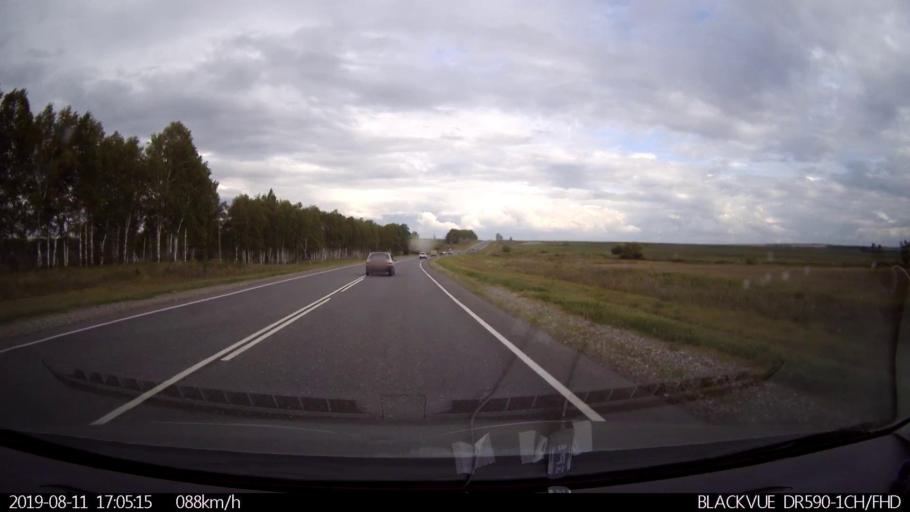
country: RU
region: Ulyanovsk
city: Mayna
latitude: 54.2991
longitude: 47.7819
